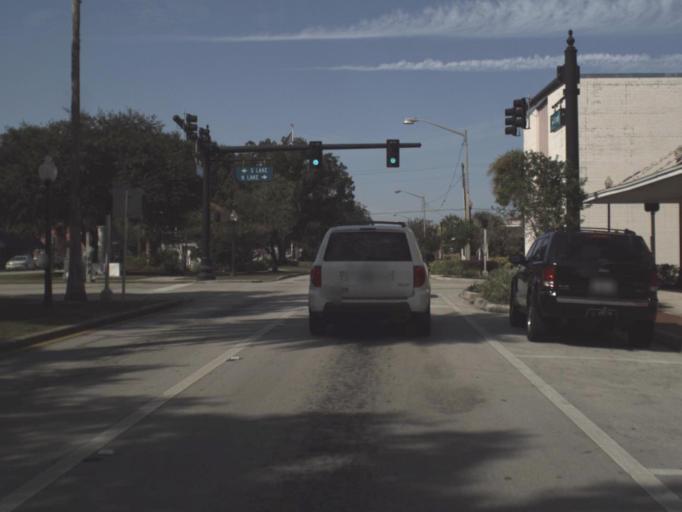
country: US
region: Florida
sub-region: Highlands County
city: Avon Park
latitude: 27.5959
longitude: -81.5018
